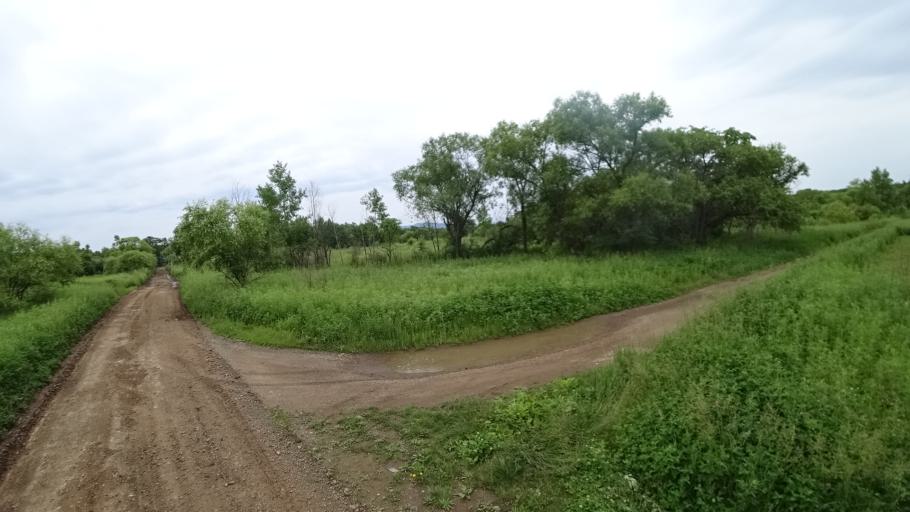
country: RU
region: Primorskiy
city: Novosysoyevka
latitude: 44.2081
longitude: 133.3286
